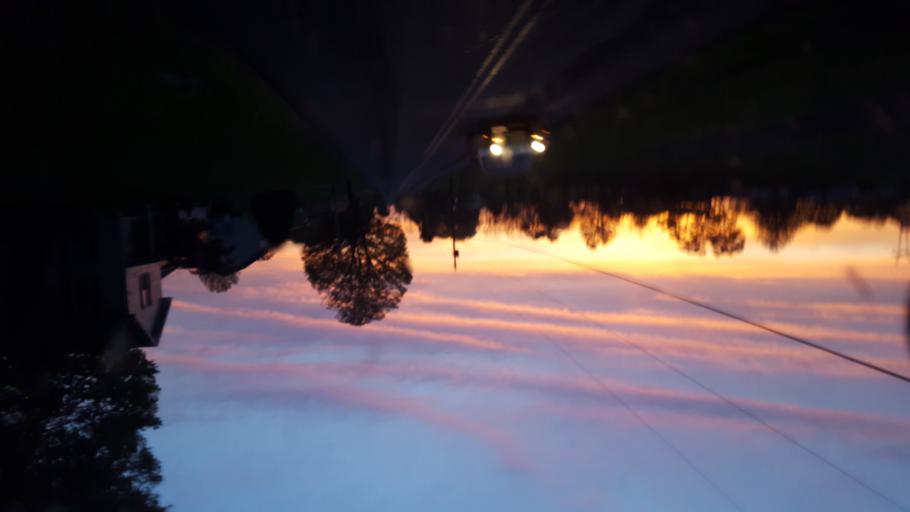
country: US
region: Ohio
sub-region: Knox County
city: Fredericktown
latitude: 40.4786
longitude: -82.5223
